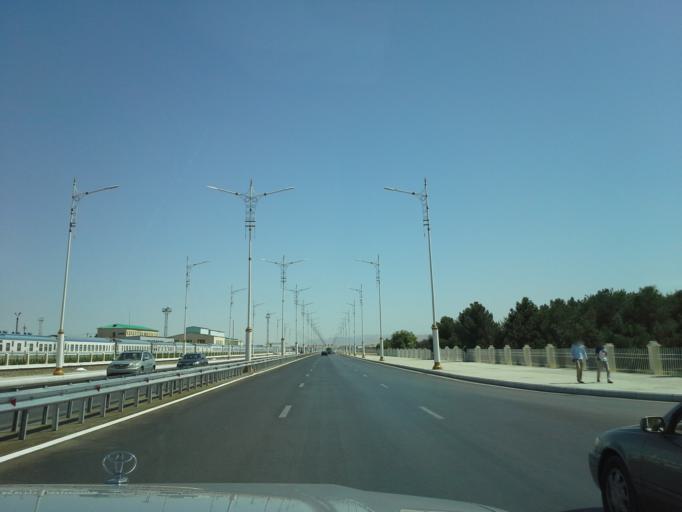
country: TM
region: Ahal
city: Ashgabat
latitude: 37.9368
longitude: 58.4074
